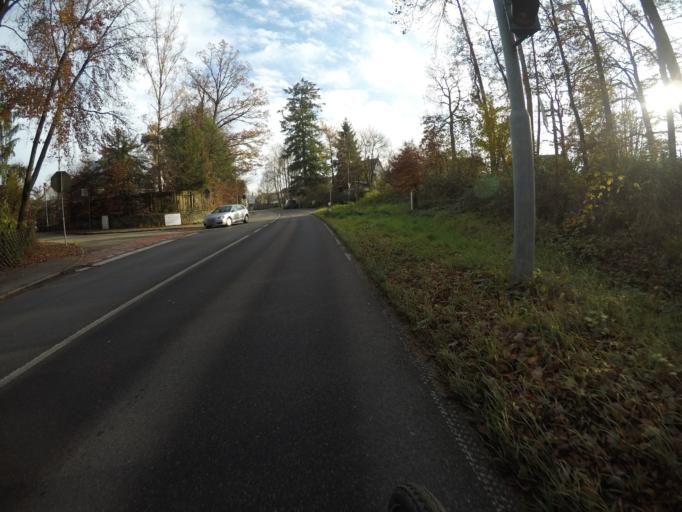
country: DE
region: Baden-Wuerttemberg
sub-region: Regierungsbezirk Stuttgart
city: Steinenbronn
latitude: 48.7069
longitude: 9.1104
